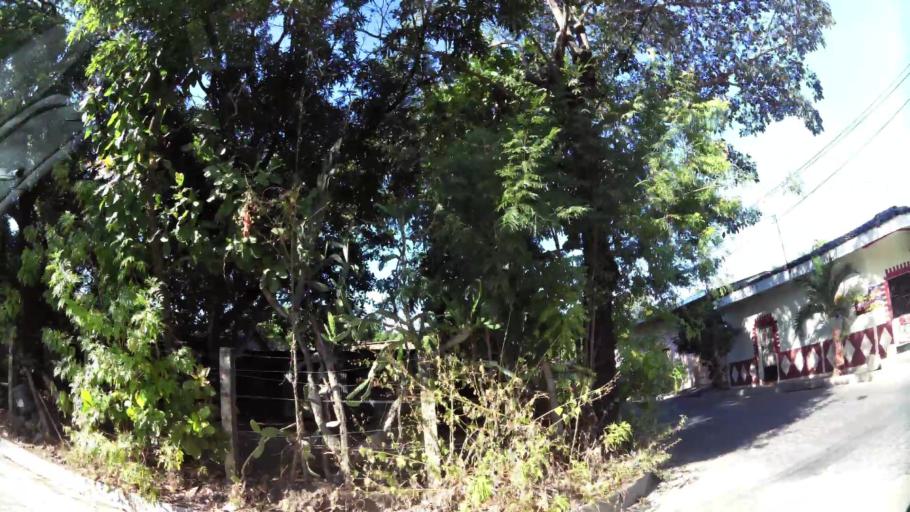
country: SV
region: San Miguel
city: San Miguel
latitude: 13.4808
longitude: -88.1939
